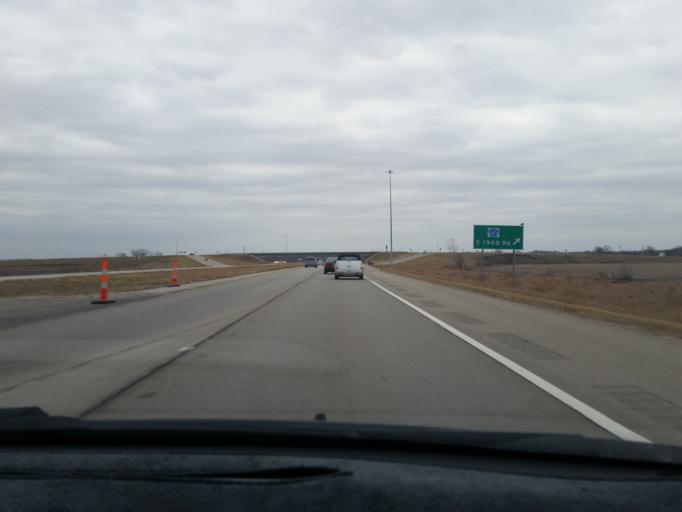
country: US
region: Kansas
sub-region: Douglas County
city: Eudora
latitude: 38.9352
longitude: -95.1550
